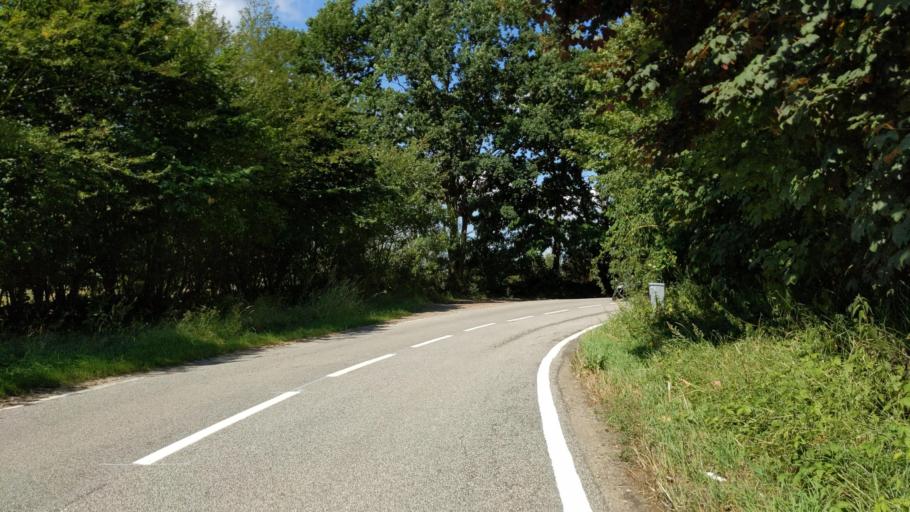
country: DE
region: Schleswig-Holstein
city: Krummesse
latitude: 53.8049
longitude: 10.6857
